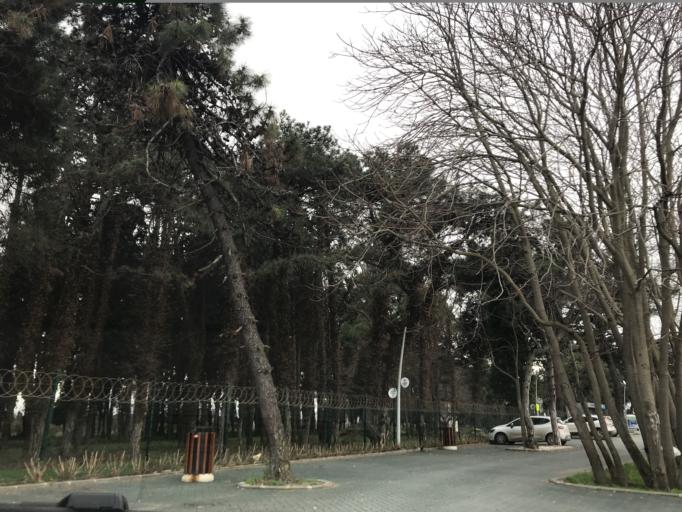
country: TR
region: Yalova
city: Yalova
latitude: 40.6648
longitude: 29.2990
